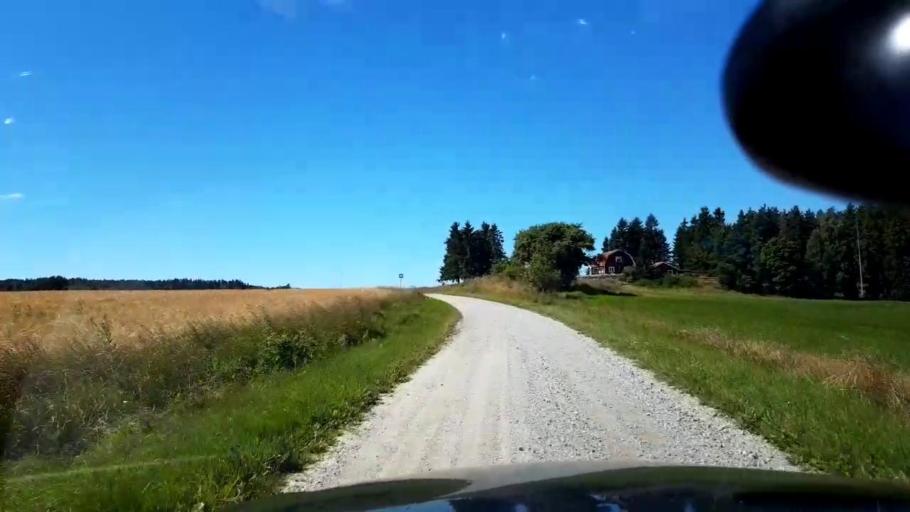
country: SE
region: Stockholm
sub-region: Sigtuna Kommun
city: Sigtuna
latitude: 59.6169
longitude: 17.6301
